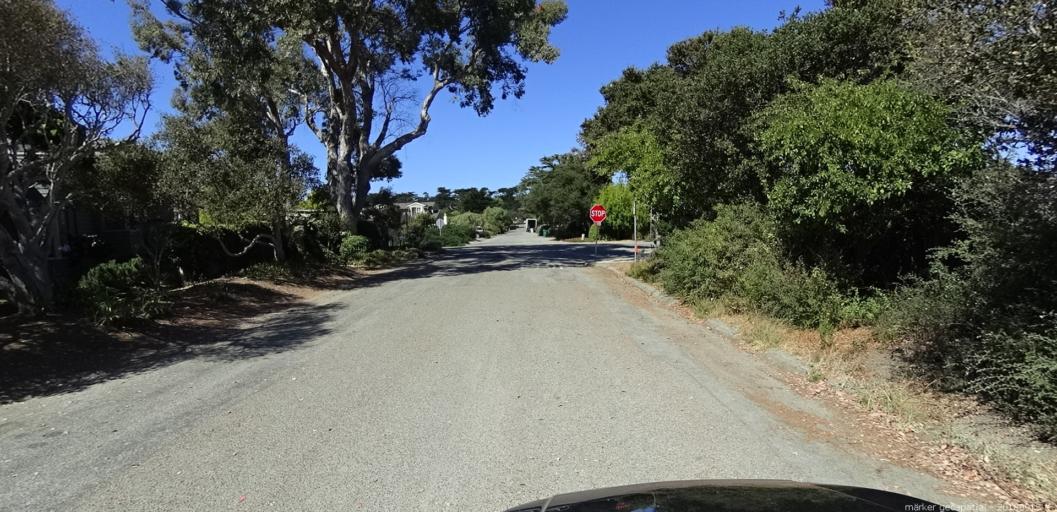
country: US
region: California
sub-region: Monterey County
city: Carmel-by-the-Sea
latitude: 36.5417
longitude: -121.9250
